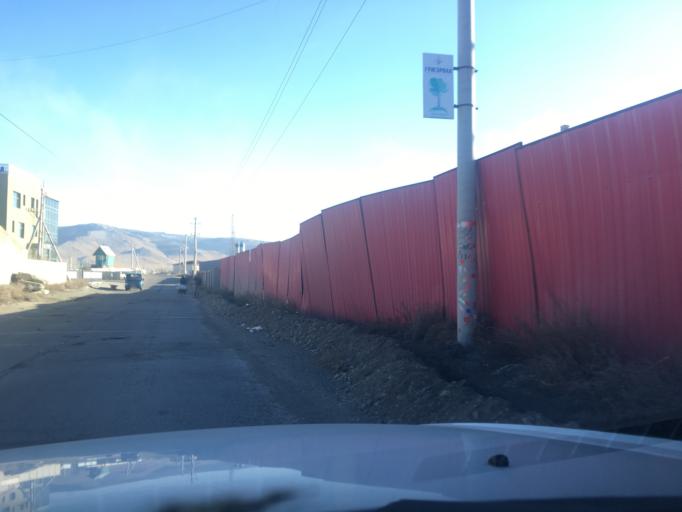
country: MN
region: Ulaanbaatar
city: Ulaanbaatar
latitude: 47.9037
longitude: 106.8038
